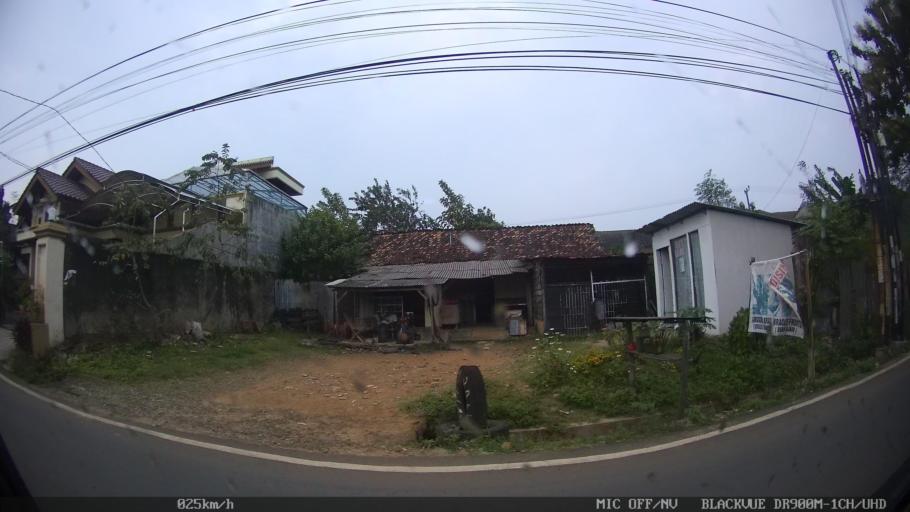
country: ID
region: Lampung
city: Kedaton
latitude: -5.3986
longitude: 105.2782
